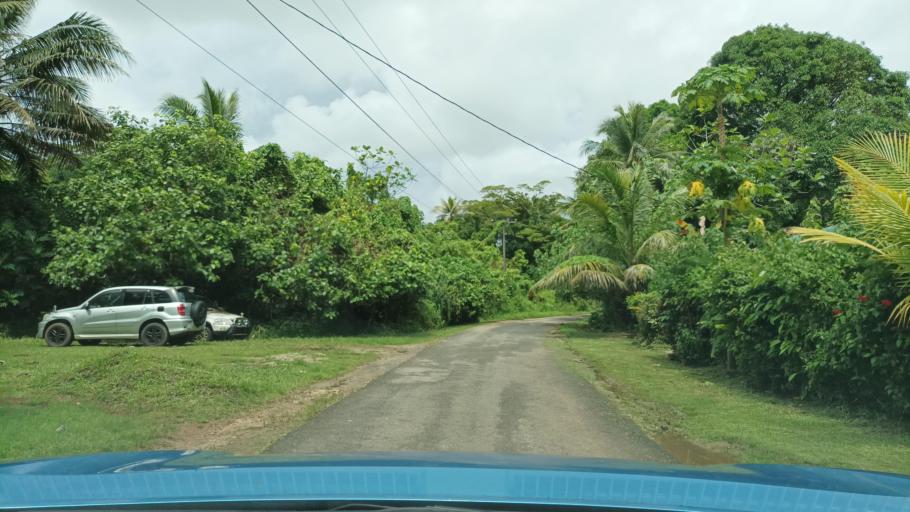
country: FM
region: Pohnpei
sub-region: Madolenihm Municipality
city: Madolenihm Municipality Government
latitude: 6.8865
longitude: 158.3165
